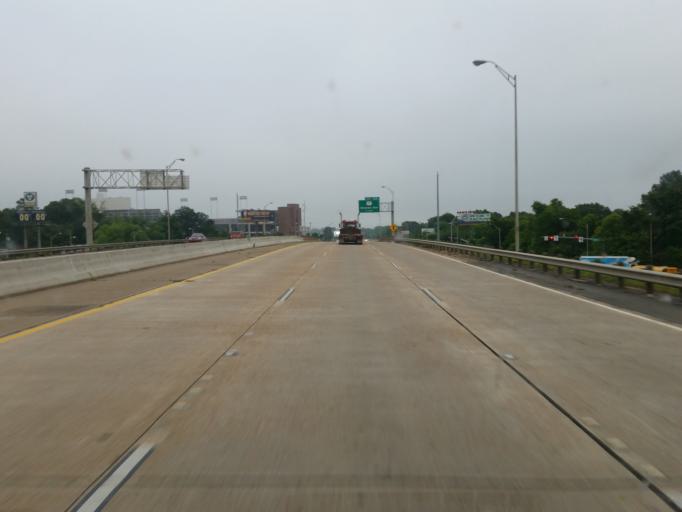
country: US
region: Louisiana
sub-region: Caddo Parish
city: Shreveport
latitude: 32.4717
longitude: -93.7987
